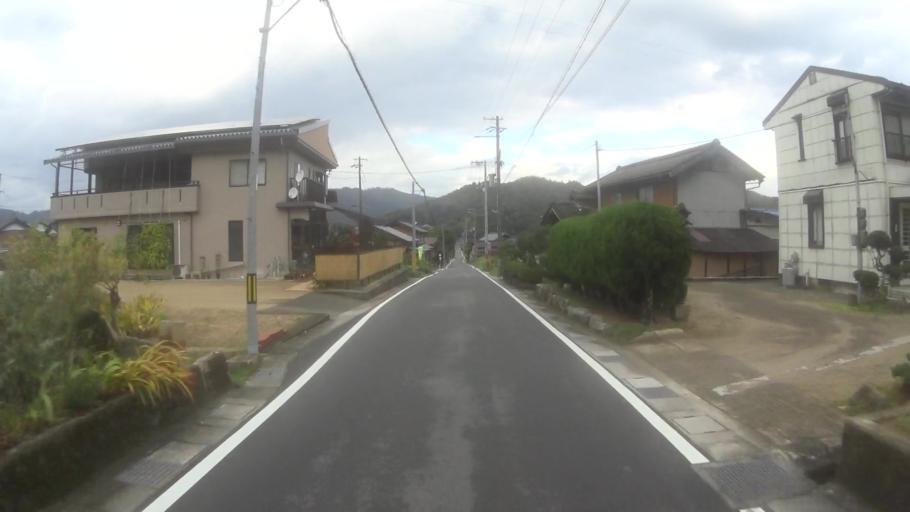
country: JP
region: Kyoto
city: Miyazu
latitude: 35.5225
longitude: 135.1259
